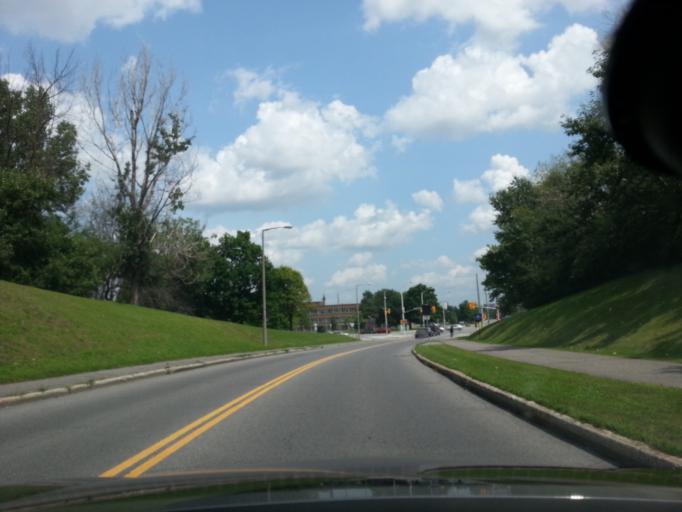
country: CA
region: Ontario
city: Ottawa
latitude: 45.3728
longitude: -75.6927
